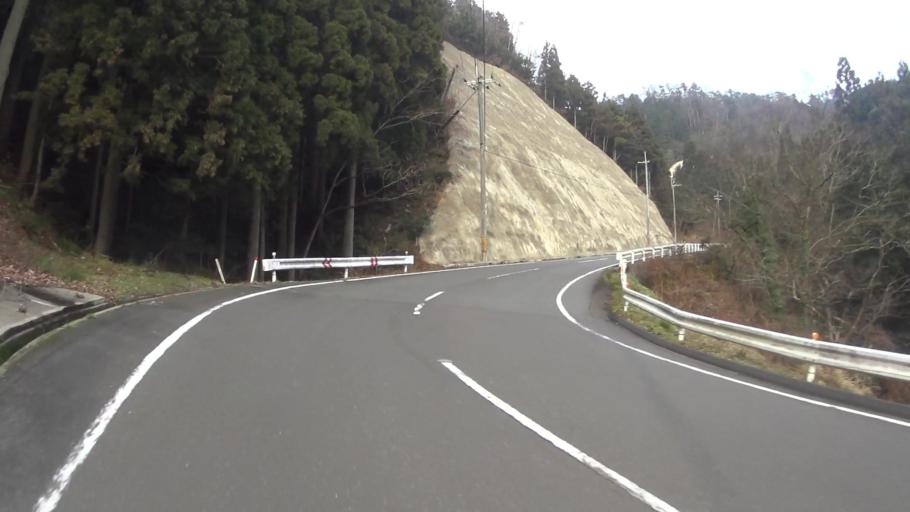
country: JP
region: Kyoto
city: Maizuru
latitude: 35.4354
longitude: 135.3931
